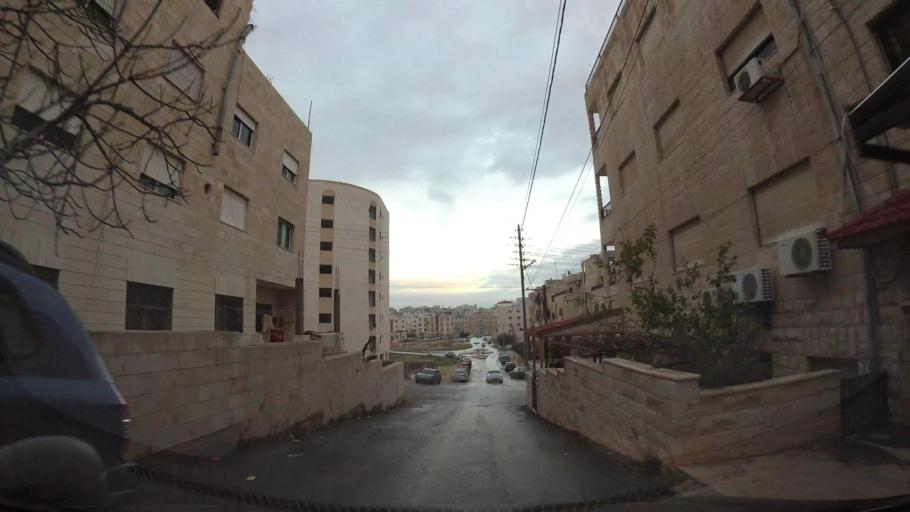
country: JO
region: Amman
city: Amman
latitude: 31.9812
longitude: 35.9120
